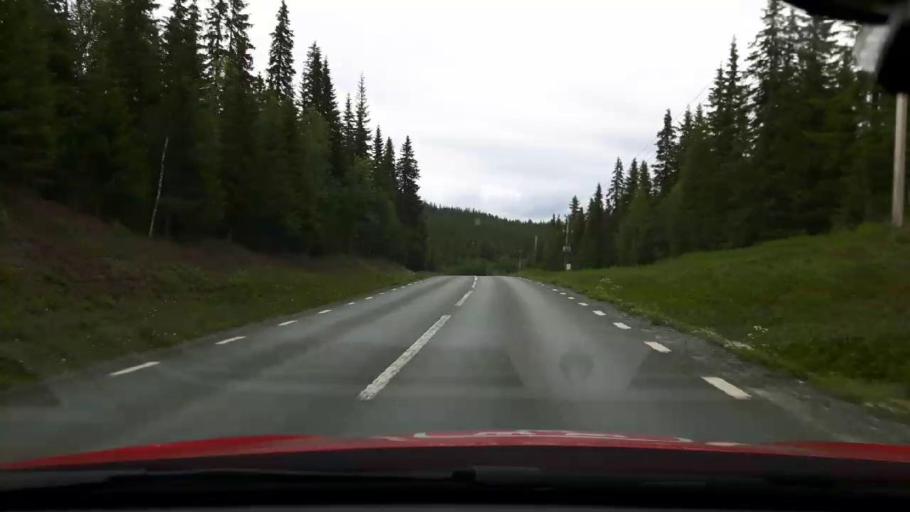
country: SE
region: Jaemtland
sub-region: Are Kommun
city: Are
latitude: 63.3792
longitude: 12.7349
